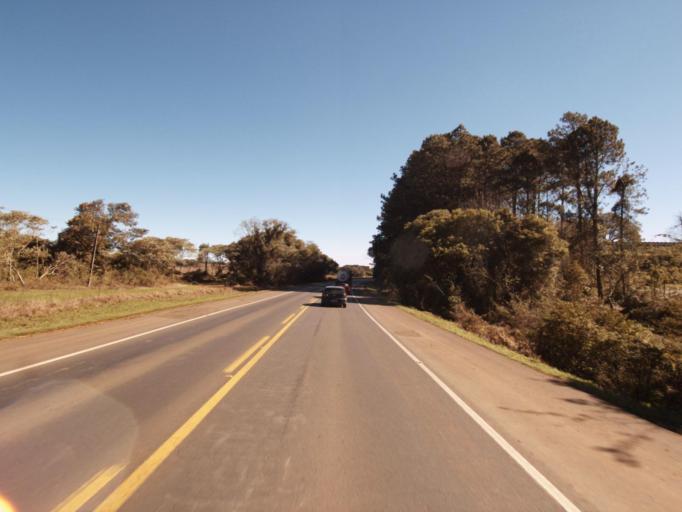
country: BR
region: Santa Catarina
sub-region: Xanxere
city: Xanxere
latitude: -26.8724
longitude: -52.2949
